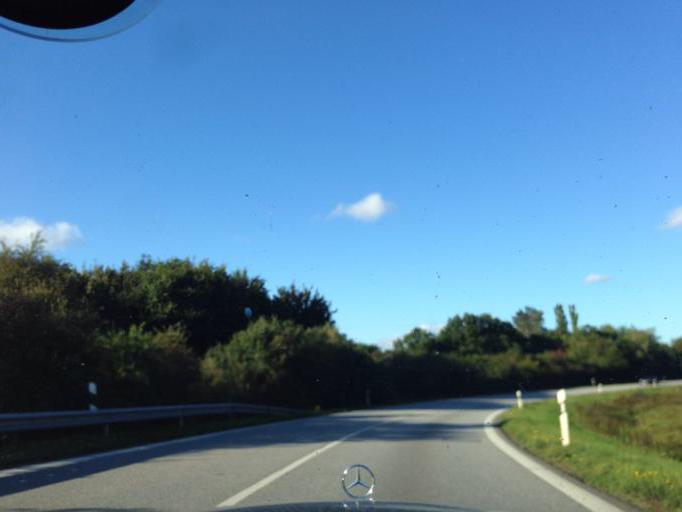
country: DE
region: Schleswig-Holstein
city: Padenstedt
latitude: 54.0423
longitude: 9.9284
